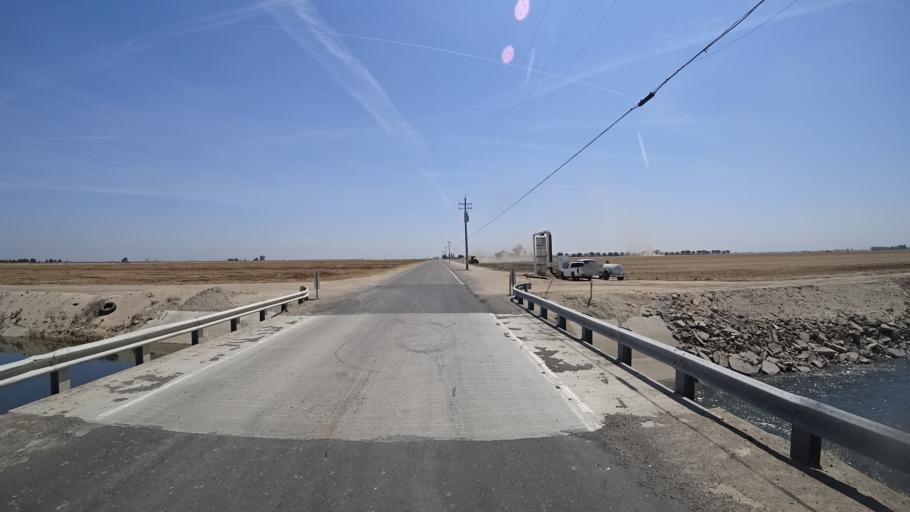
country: US
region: California
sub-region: Fresno County
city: Kingsburg
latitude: 36.4014
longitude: -119.5378
